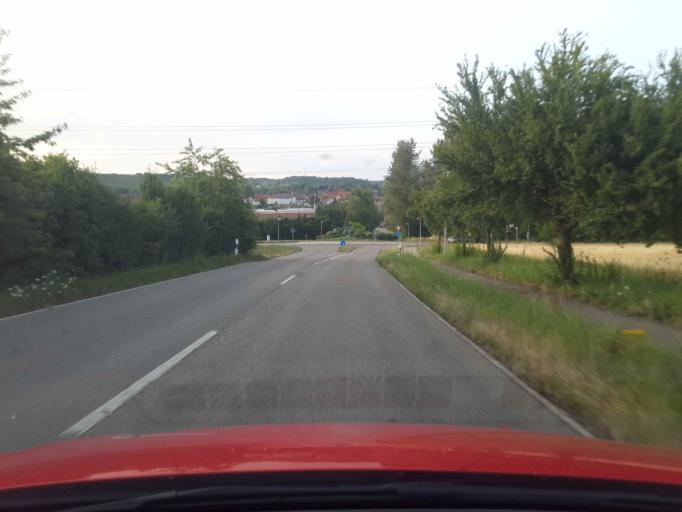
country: DE
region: Baden-Wuerttemberg
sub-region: Regierungsbezirk Stuttgart
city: Guglingen
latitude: 49.0601
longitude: 8.9976
